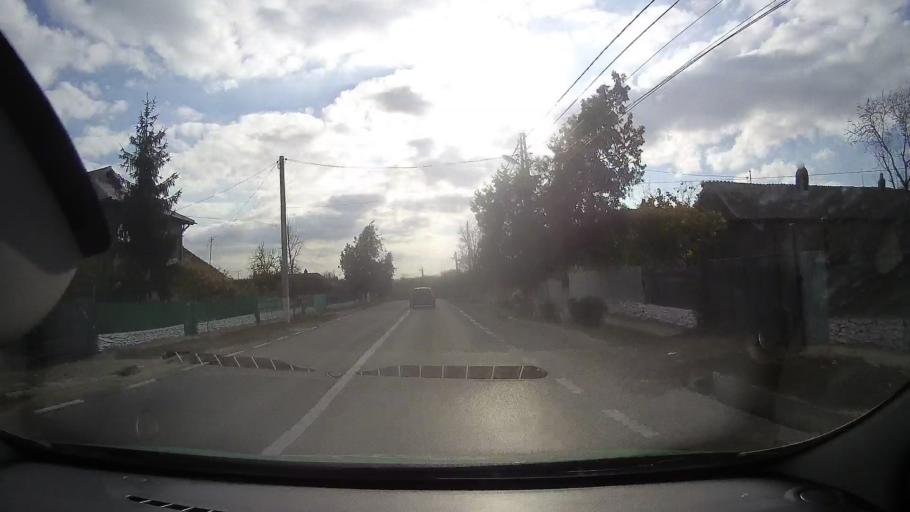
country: RO
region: Tulcea
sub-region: Comuna Topolog
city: Topolog
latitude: 44.8771
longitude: 28.3745
